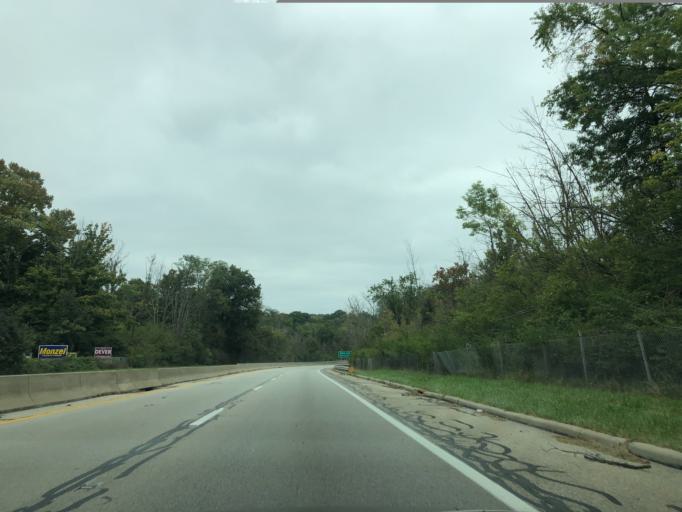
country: US
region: Ohio
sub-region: Hamilton County
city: Dillonvale
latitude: 39.2190
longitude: -84.4189
